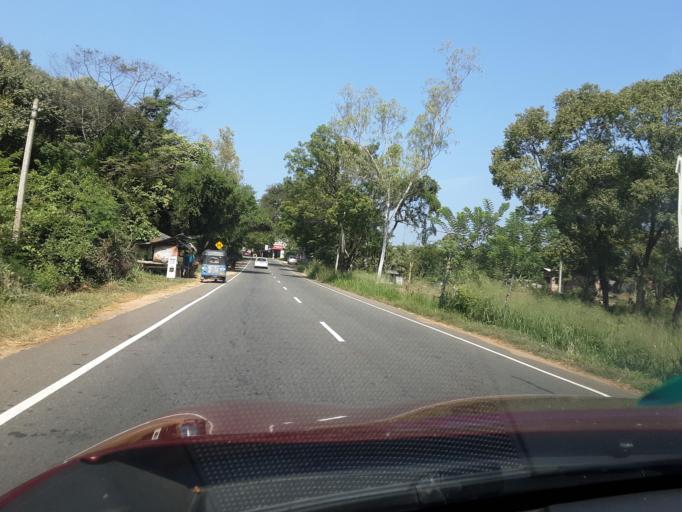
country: LK
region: Uva
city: Badulla
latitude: 7.2839
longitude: 81.0422
